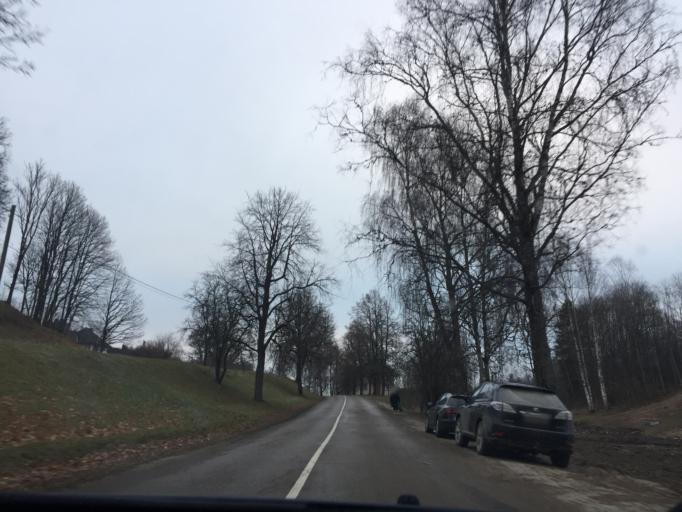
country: LV
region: Raunas
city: Rauna
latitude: 57.3290
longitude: 25.6047
